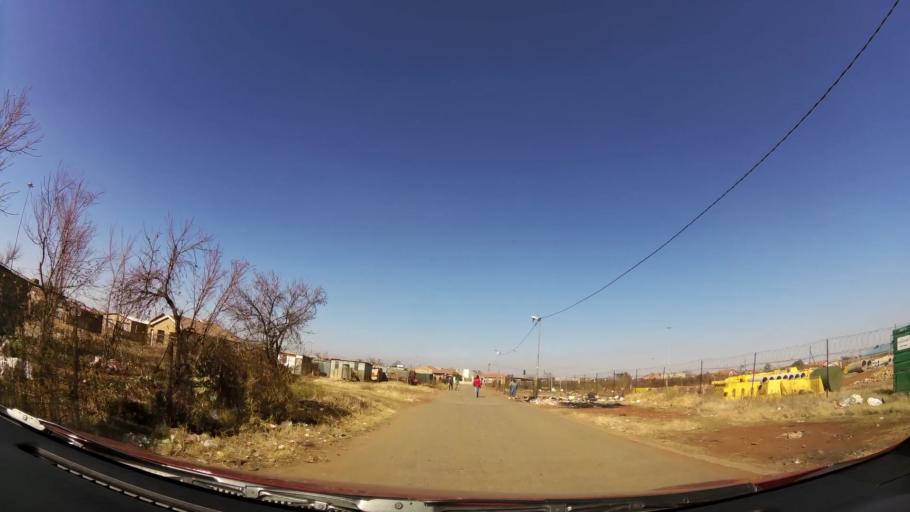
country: ZA
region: Gauteng
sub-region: City of Johannesburg Metropolitan Municipality
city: Soweto
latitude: -26.2160
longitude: 27.8295
